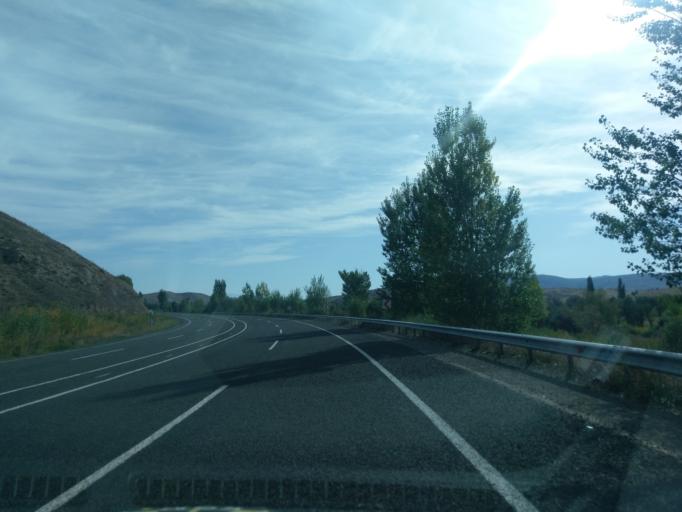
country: TR
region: Sivas
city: Zara
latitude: 39.8487
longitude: 37.8460
